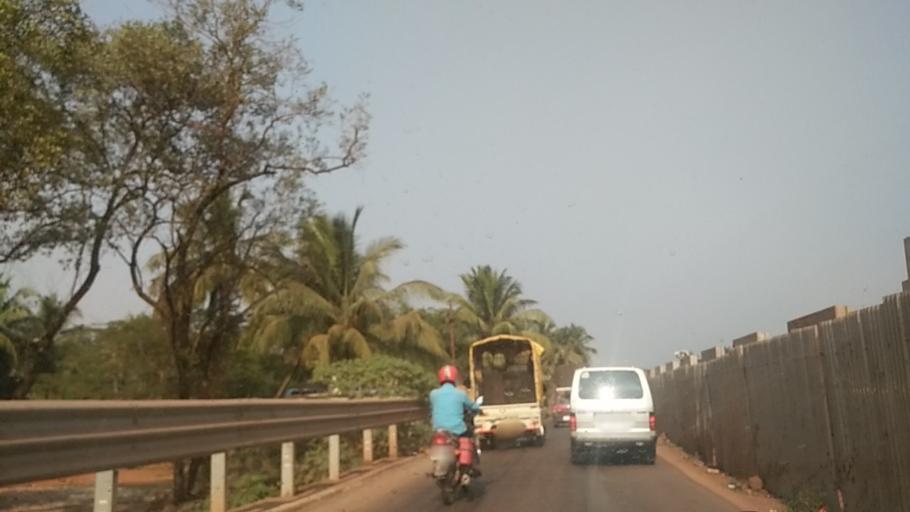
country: IN
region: Goa
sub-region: North Goa
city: Mapuca
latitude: 15.5869
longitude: 73.8193
